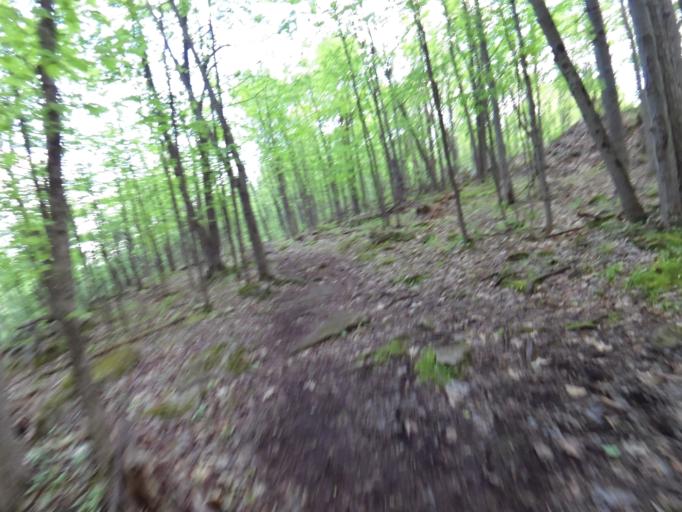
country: CA
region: Ontario
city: Bells Corners
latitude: 45.3382
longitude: -75.8651
